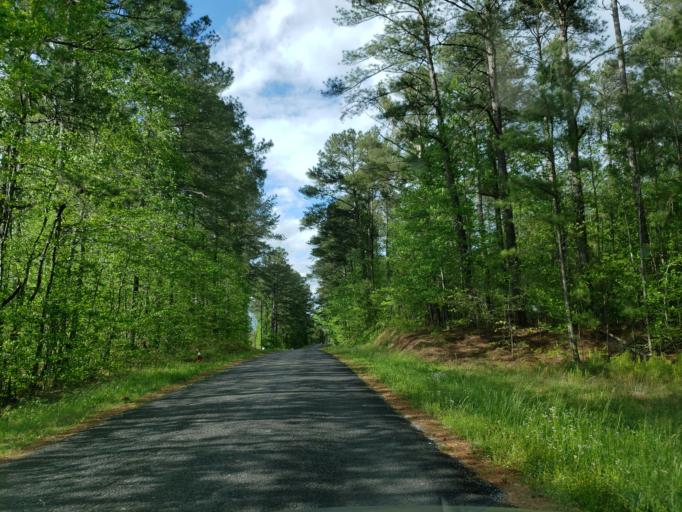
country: US
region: Georgia
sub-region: Haralson County
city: Tallapoosa
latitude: 33.7821
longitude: -85.3814
